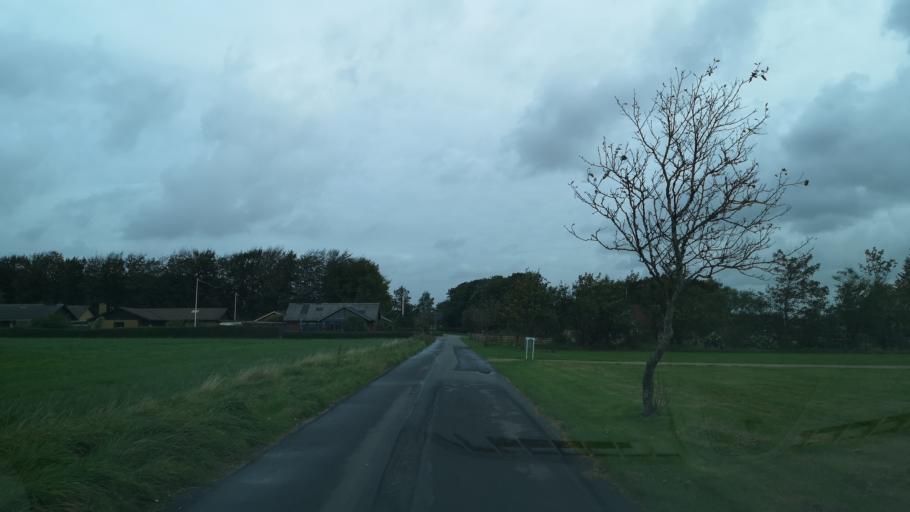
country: DK
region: Central Jutland
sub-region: Ringkobing-Skjern Kommune
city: Skjern
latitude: 55.9815
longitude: 8.5469
